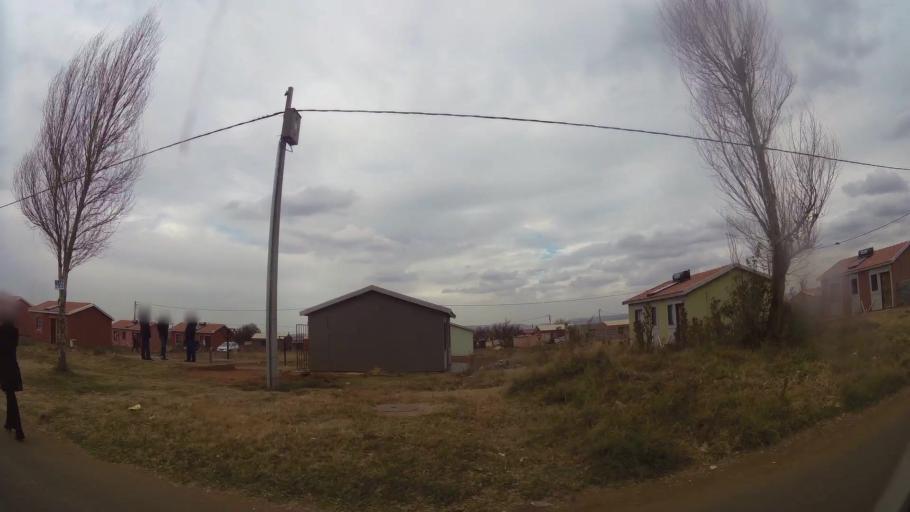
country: ZA
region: Gauteng
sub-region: Ekurhuleni Metropolitan Municipality
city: Germiston
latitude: -26.3946
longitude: 28.1523
